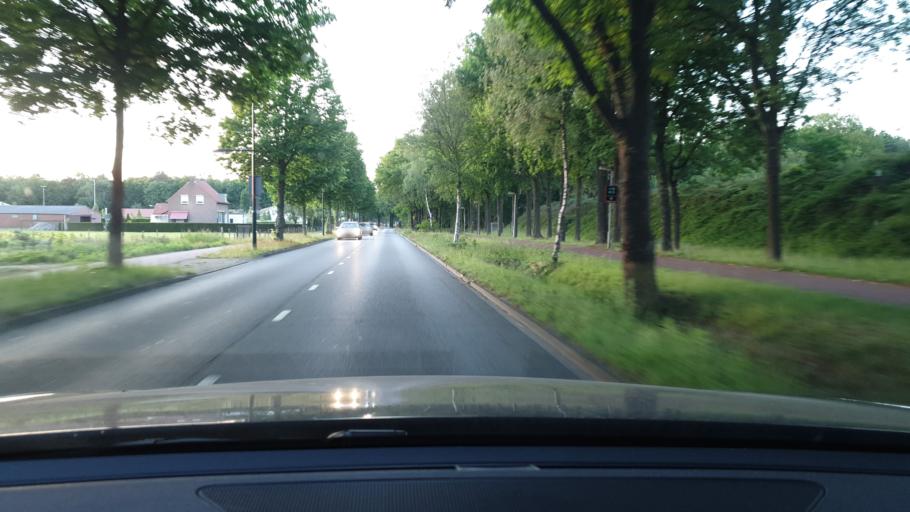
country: NL
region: North Brabant
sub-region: Gemeente Valkenswaard
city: Valkenswaard
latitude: 51.3657
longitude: 5.4457
